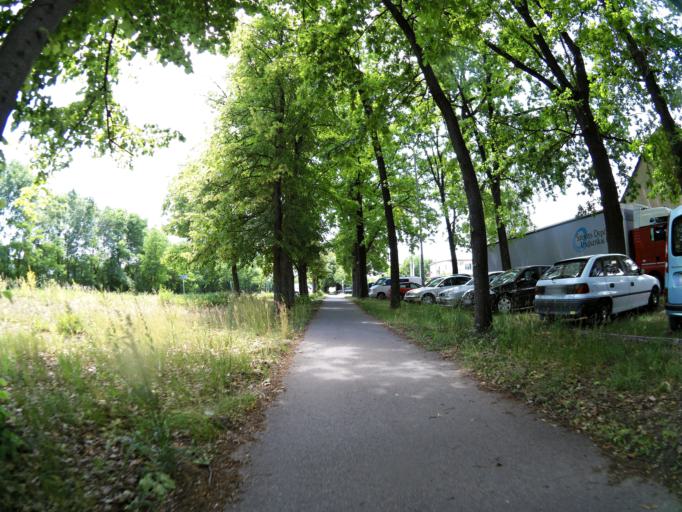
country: HU
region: Csongrad
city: Kistelek
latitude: 46.4769
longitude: 19.9956
